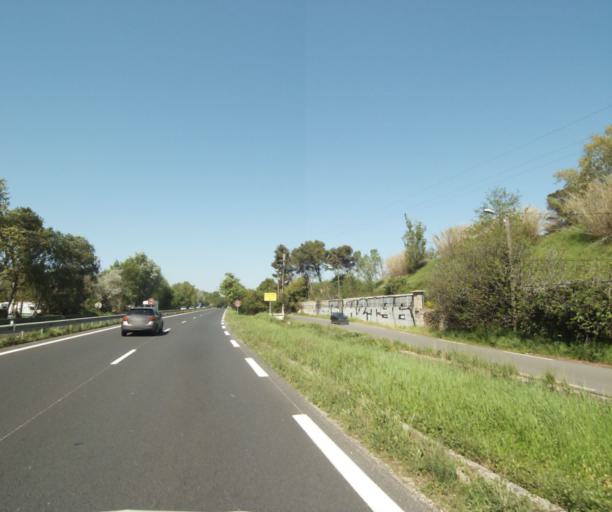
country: FR
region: Languedoc-Roussillon
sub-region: Departement de l'Herault
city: Juvignac
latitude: 43.6023
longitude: 3.8198
